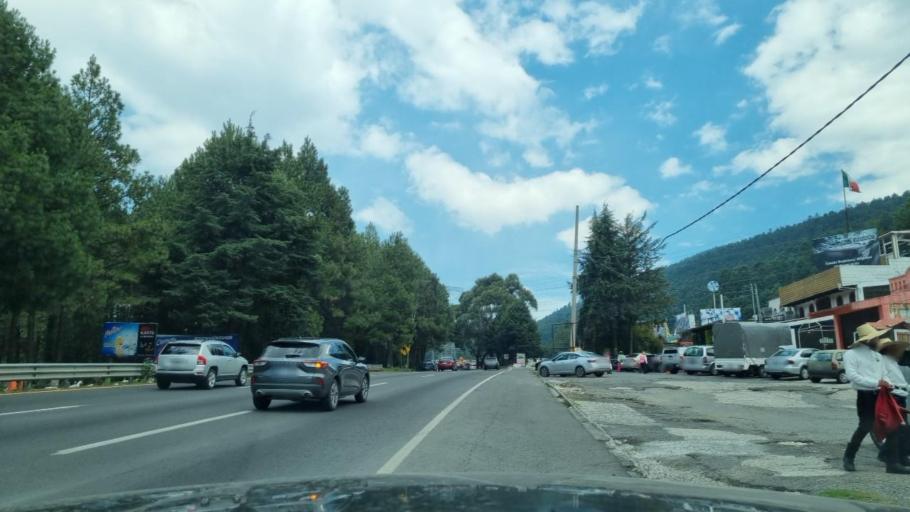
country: MX
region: Morelos
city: San Jeronimo Acazulco
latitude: 19.2971
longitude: -99.4017
